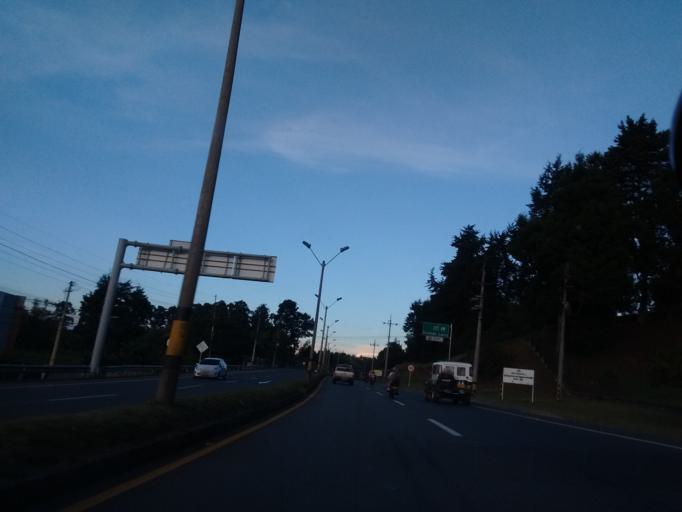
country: CO
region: Antioquia
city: Rionegro
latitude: 6.1792
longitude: -75.3659
